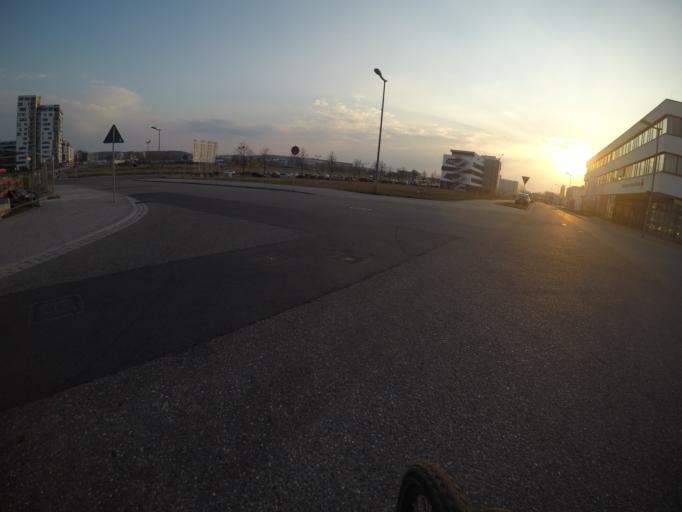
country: DE
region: Baden-Wuerttemberg
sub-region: Regierungsbezirk Stuttgart
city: Boeblingen
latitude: 48.6906
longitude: 8.9942
